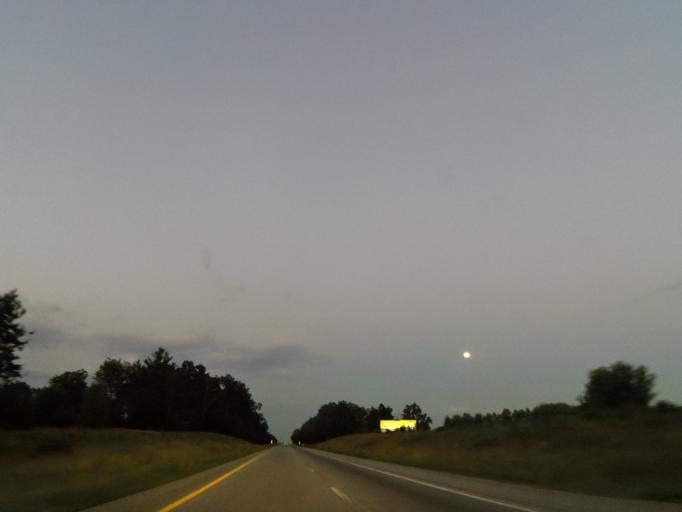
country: US
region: Tennessee
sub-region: Putnam County
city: Monterey
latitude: 36.0520
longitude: -85.1658
